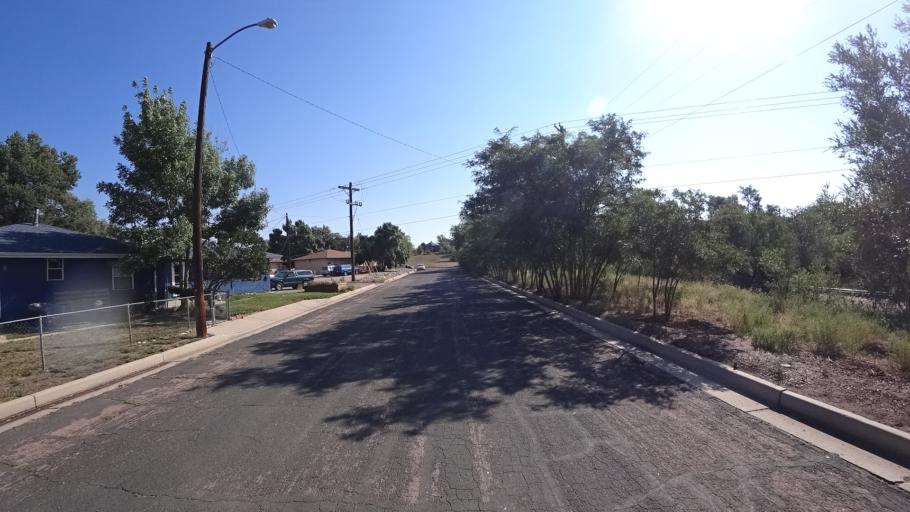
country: US
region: Colorado
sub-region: El Paso County
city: Colorado Springs
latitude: 38.8690
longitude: -104.8253
